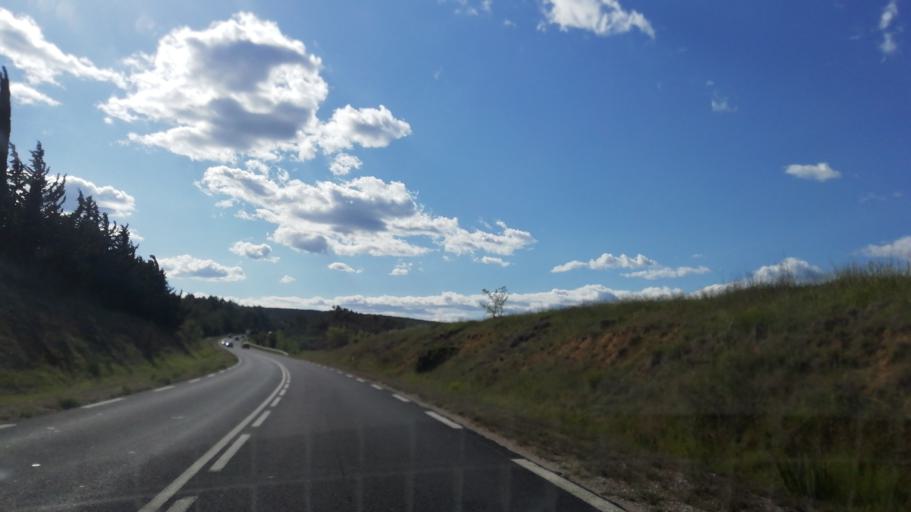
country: FR
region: Languedoc-Roussillon
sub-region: Departement de l'Herault
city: Saint-Gely-du-Fesc
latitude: 43.7087
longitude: 3.8069
